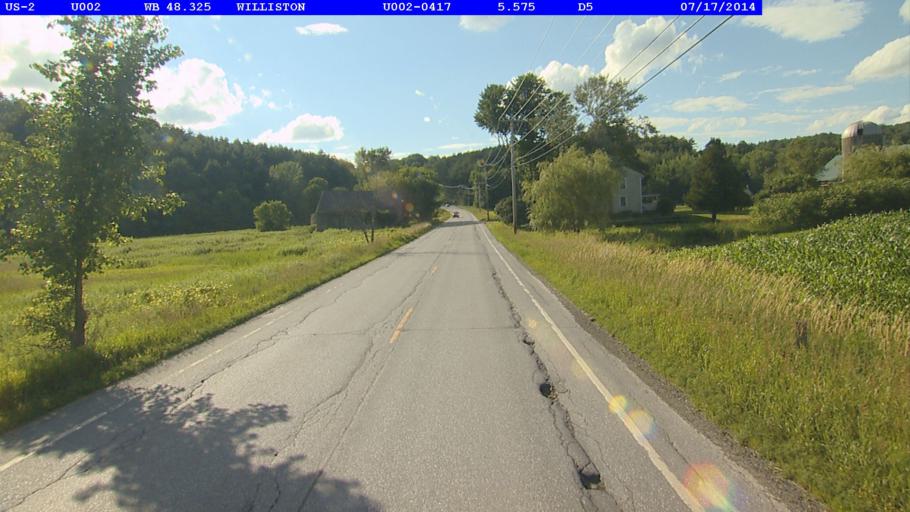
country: US
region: Vermont
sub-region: Chittenden County
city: Williston
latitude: 44.4321
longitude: -73.0334
